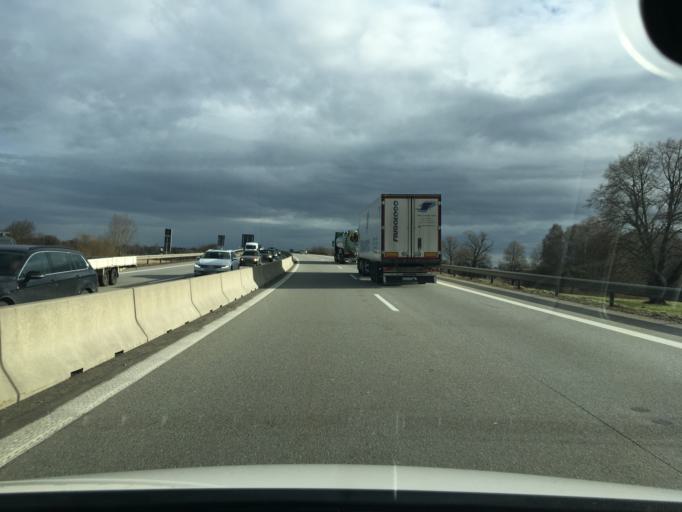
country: DE
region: Bavaria
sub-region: Upper Bavaria
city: Bernau am Chiemsee
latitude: 47.8172
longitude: 12.3714
